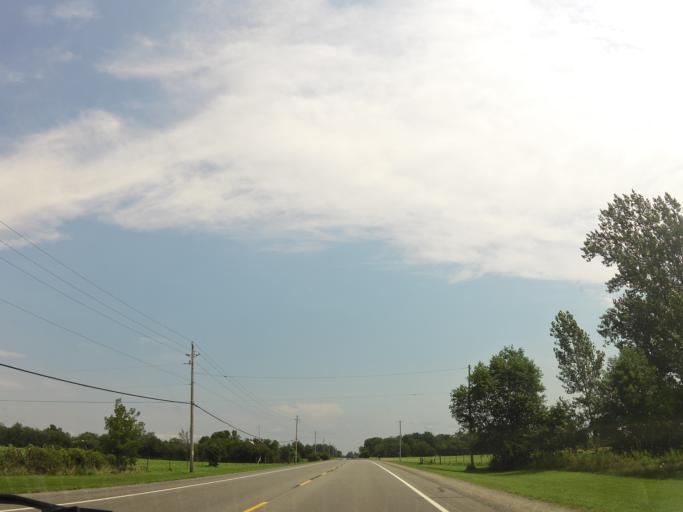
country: CA
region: Ontario
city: Kingston
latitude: 44.4071
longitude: -76.5508
